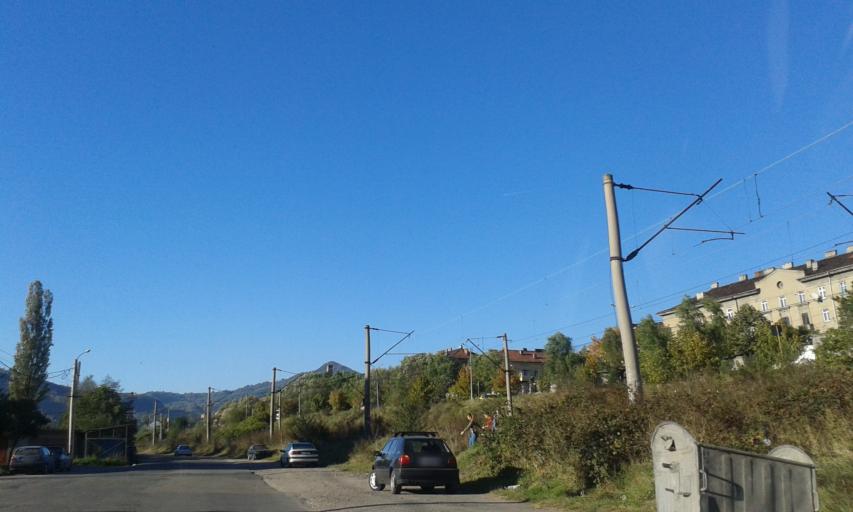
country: RO
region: Hunedoara
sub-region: Municipiul Petrosani
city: Petrosani
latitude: 45.4098
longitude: 23.3707
